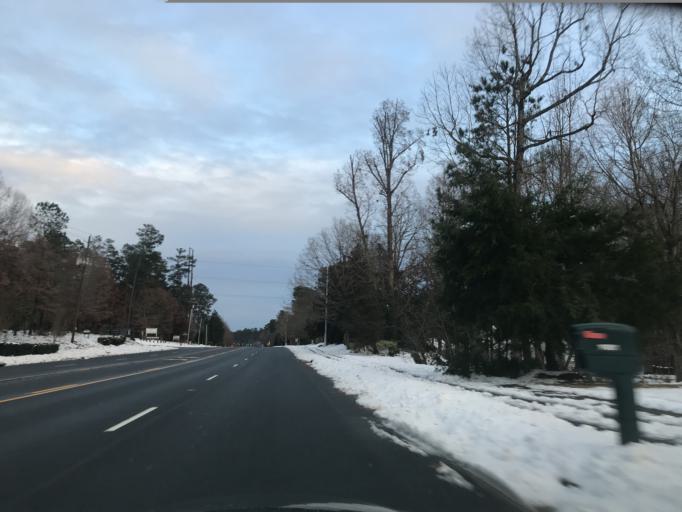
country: US
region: North Carolina
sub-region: Wake County
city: Wake Forest
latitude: 35.9071
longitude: -78.5960
